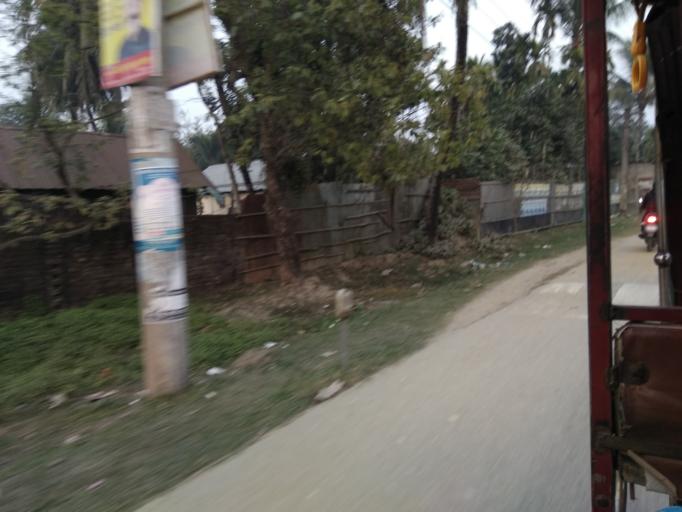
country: BD
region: Dhaka
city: Netrakona
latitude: 24.8695
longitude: 90.7087
